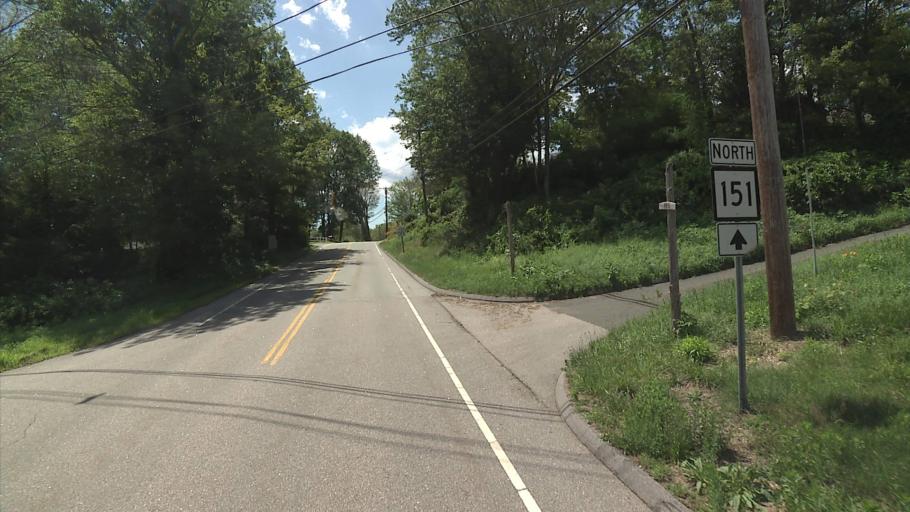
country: US
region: Connecticut
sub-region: Middlesex County
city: Moodus
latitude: 41.5016
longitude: -72.4564
